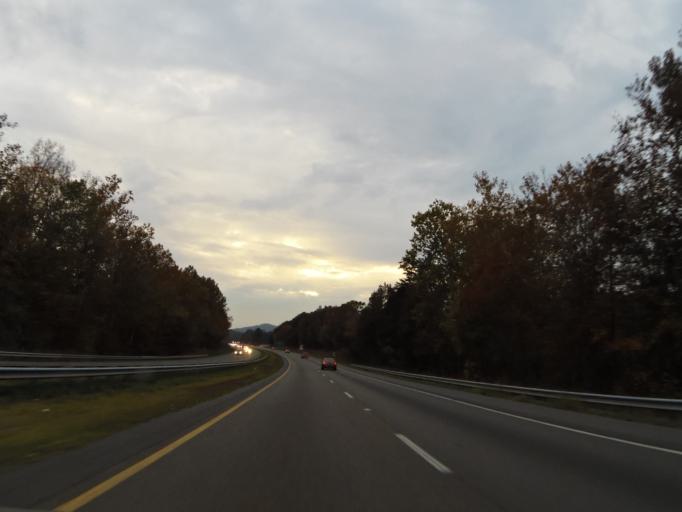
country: US
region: North Carolina
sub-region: Burke County
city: Rutherford College
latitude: 35.7323
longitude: -81.5376
